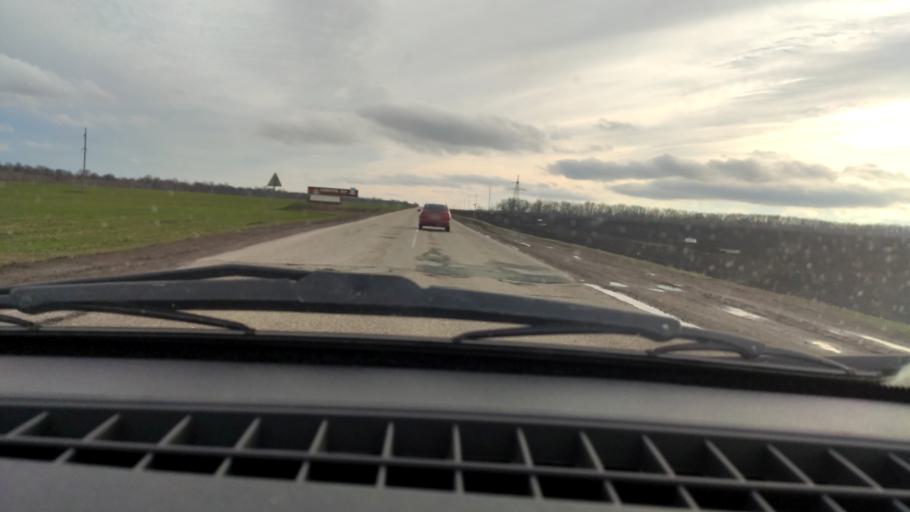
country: RU
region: Bashkortostan
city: Chishmy
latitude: 54.5624
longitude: 55.3455
